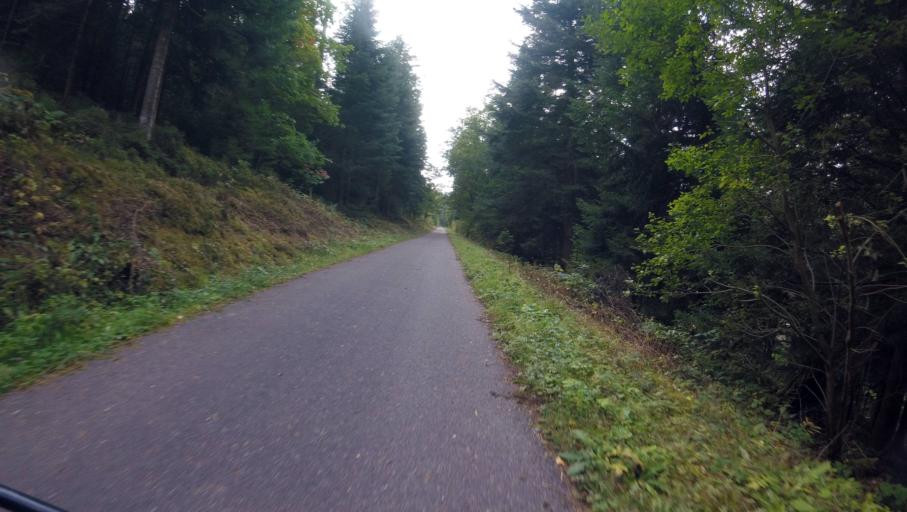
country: DE
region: Baden-Wuerttemberg
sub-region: Karlsruhe Region
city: Altensteig
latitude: 48.5861
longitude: 8.5838
